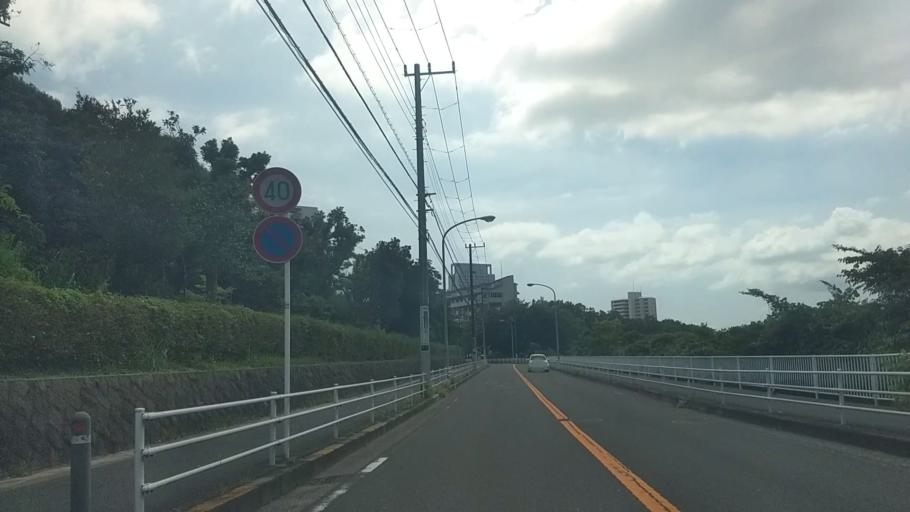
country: JP
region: Kanagawa
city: Yokosuka
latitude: 35.3573
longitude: 139.6371
